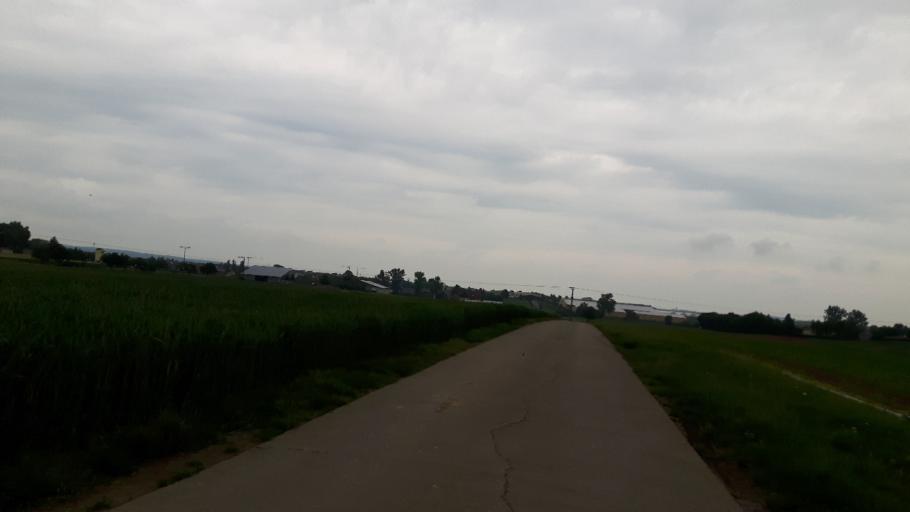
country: DE
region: Bavaria
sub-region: Regierungsbezirk Unterfranken
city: Unterpleichfeld
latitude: 49.8626
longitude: 10.0544
